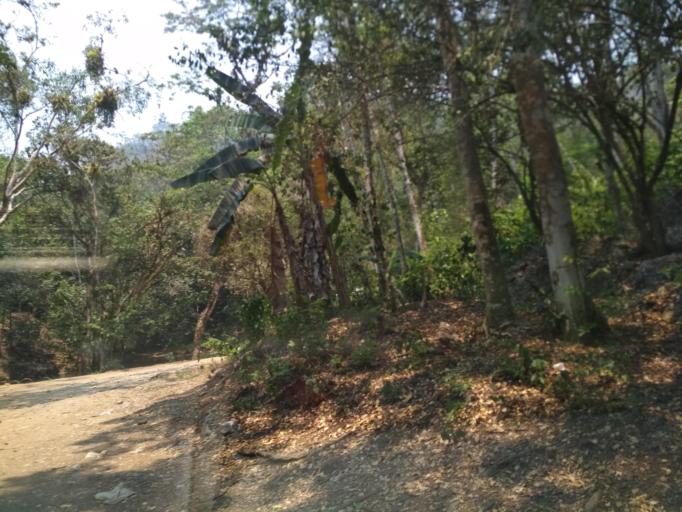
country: MX
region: Veracruz
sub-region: Tezonapa
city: Laguna Chica (Pueblo Nuevo)
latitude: 18.5716
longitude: -96.7298
